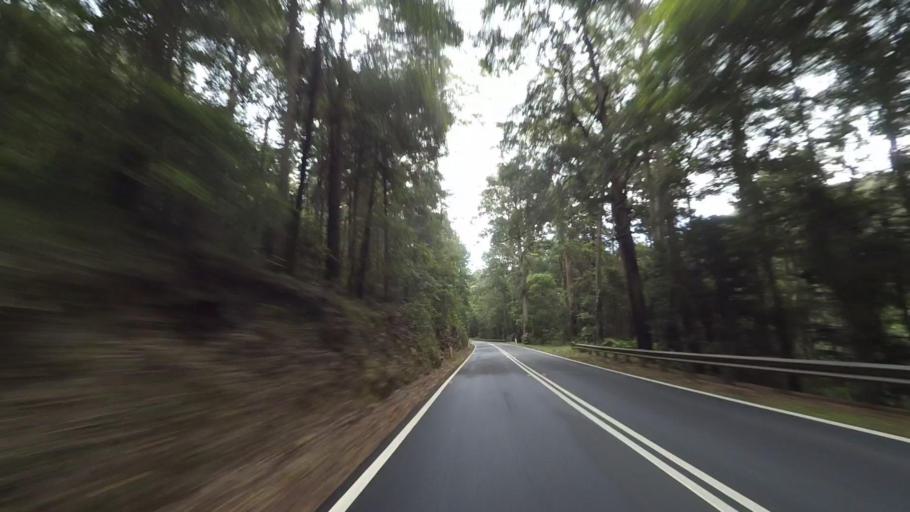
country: AU
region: New South Wales
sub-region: Wollongong
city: Helensburgh
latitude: -34.1608
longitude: 151.0163
